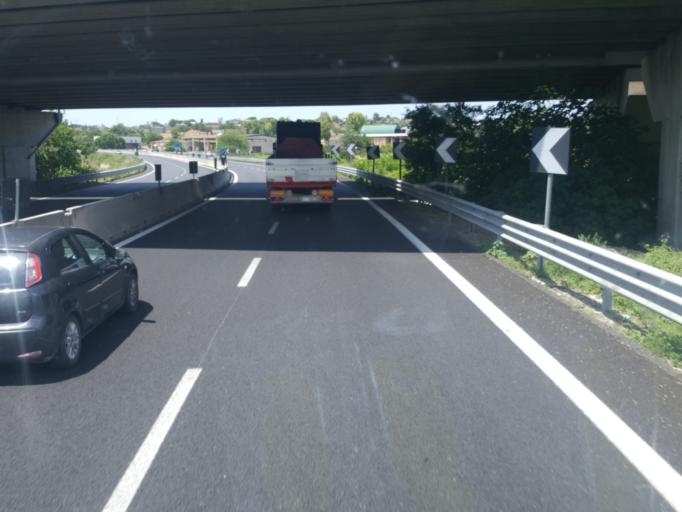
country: IT
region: Latium
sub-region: Citta metropolitana di Roma Capitale
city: Fiano Romano
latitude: 42.1497
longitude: 12.6254
